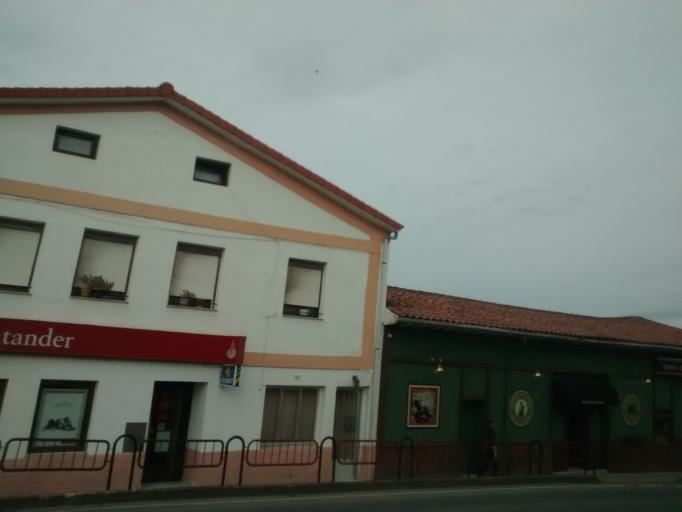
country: ES
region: Cantabria
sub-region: Provincia de Cantabria
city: Puente Viesgo
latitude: 43.3215
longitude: -3.9621
